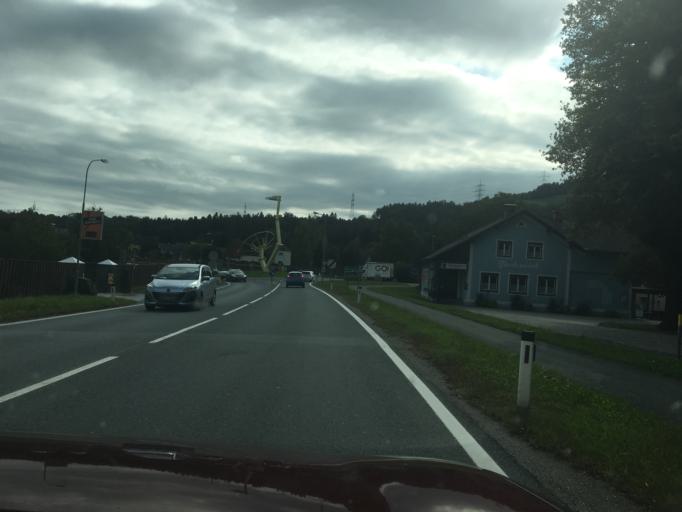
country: AT
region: Styria
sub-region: Politischer Bezirk Deutschlandsberg
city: Hollenegg
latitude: 46.8009
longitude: 15.2211
